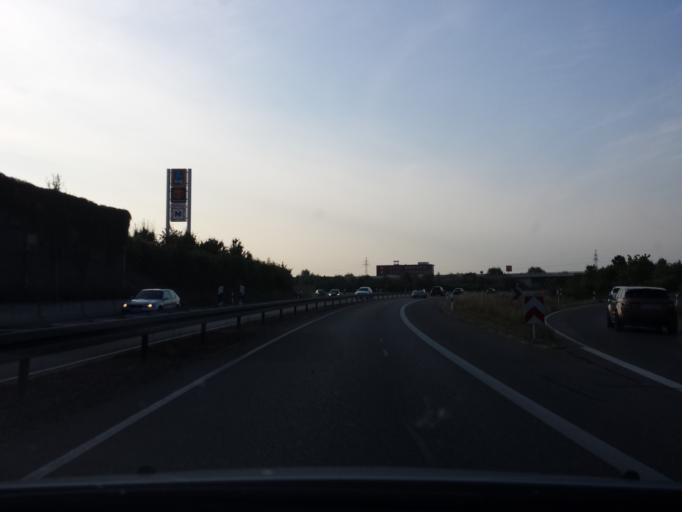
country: DE
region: Bavaria
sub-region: Swabia
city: Friedberg
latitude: 48.3614
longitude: 10.9591
